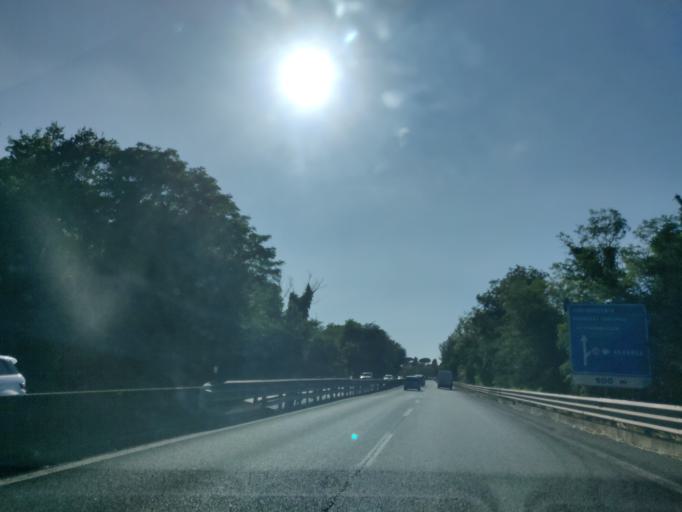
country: IT
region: Latium
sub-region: Citta metropolitana di Roma Capitale
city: Ara Nova
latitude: 41.9102
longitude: 12.2578
